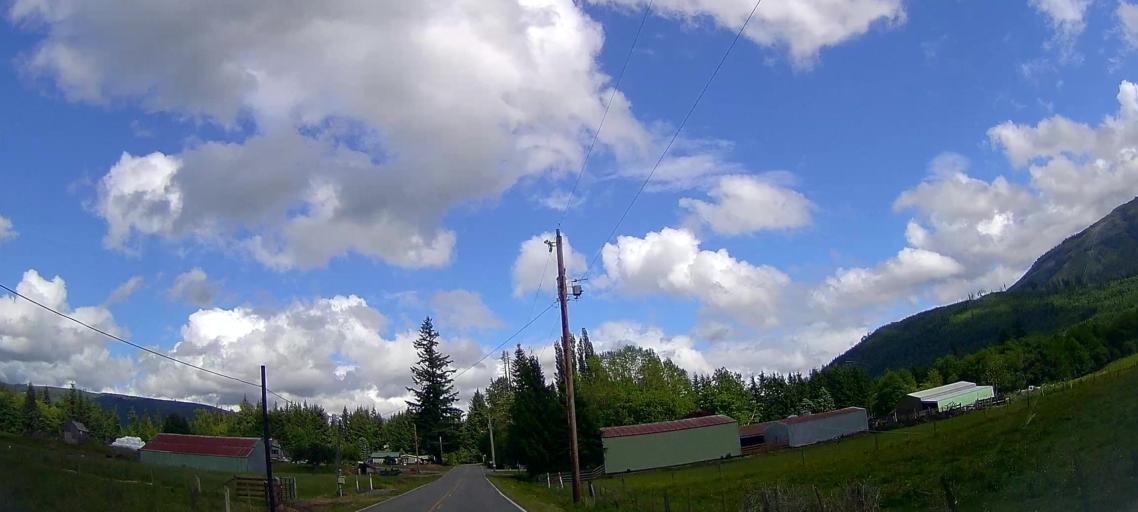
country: US
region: Washington
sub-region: Whatcom County
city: Sudden Valley
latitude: 48.6785
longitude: -122.1904
